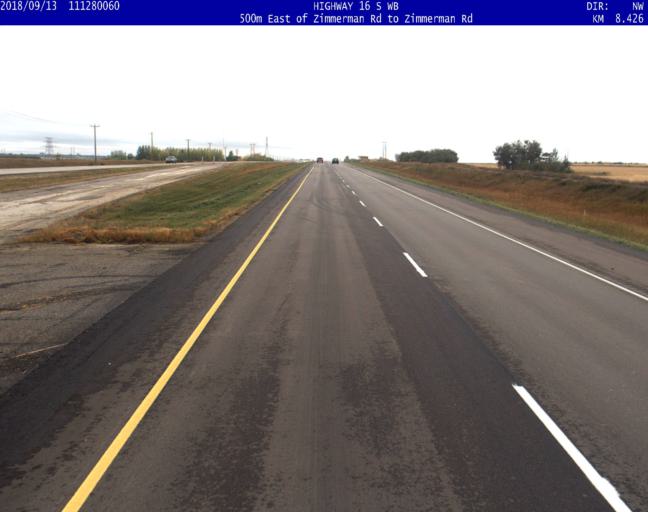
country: CA
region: Saskatchewan
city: Saskatoon
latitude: 52.0658
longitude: -106.4897
